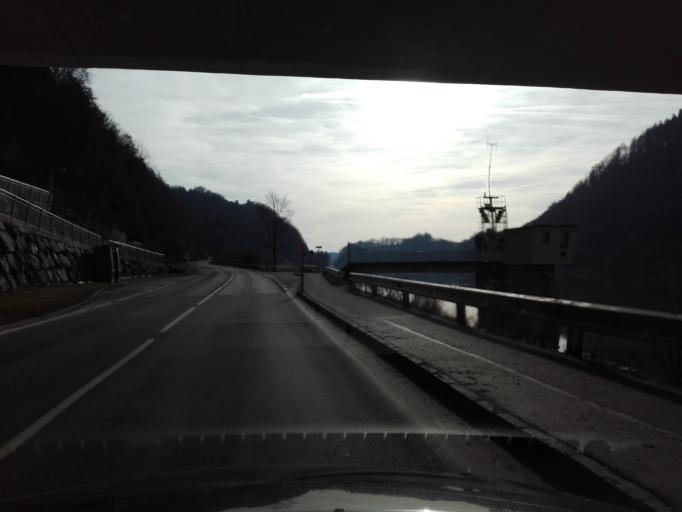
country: AT
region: Upper Austria
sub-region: Politischer Bezirk Perg
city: Bad Kreuzen
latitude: 48.2108
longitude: 14.8579
